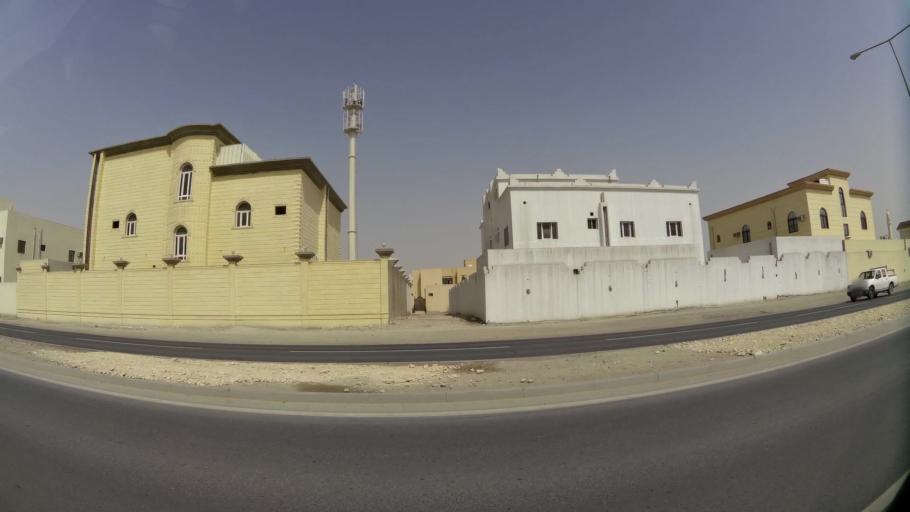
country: QA
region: Baladiyat ar Rayyan
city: Ar Rayyan
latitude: 25.2365
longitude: 51.3822
